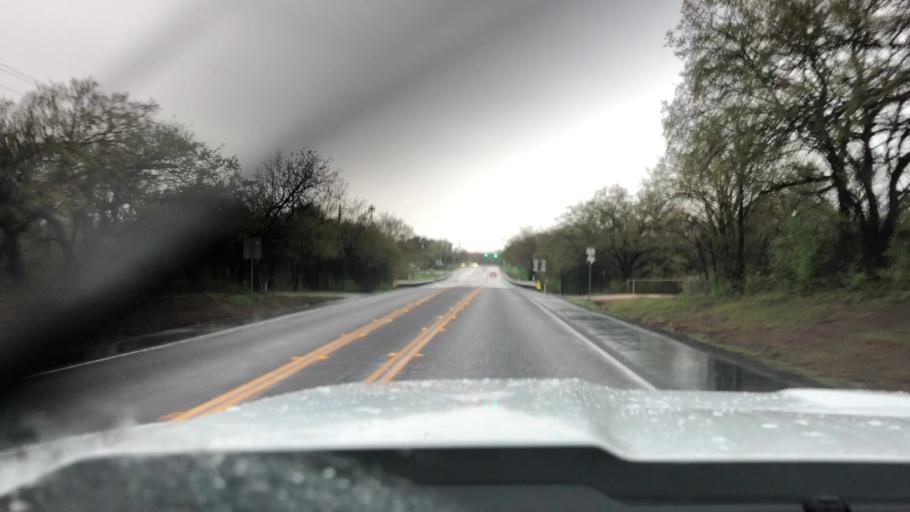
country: US
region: Texas
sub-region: Johnson County
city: Keene
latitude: 32.4154
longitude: -97.3214
